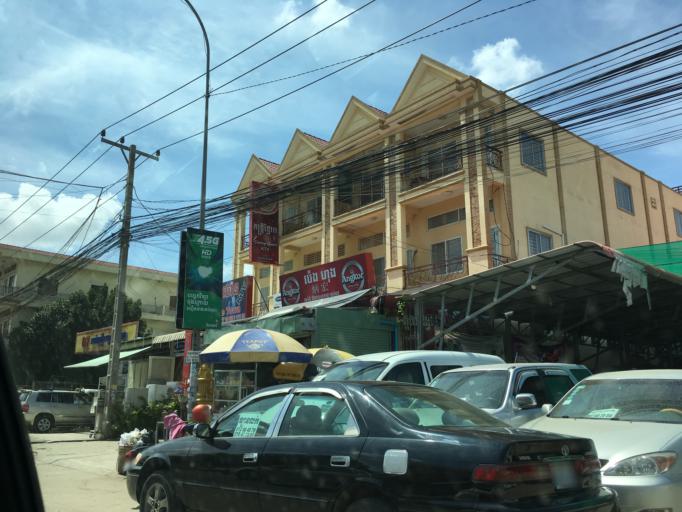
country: KH
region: Phnom Penh
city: Phnom Penh
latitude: 11.5504
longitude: 104.8593
